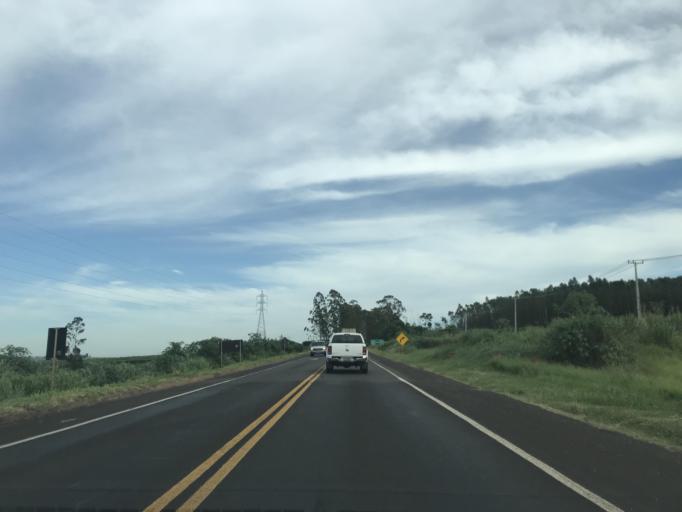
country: BR
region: Parana
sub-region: Paranavai
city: Nova Aurora
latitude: -22.9905
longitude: -52.5953
